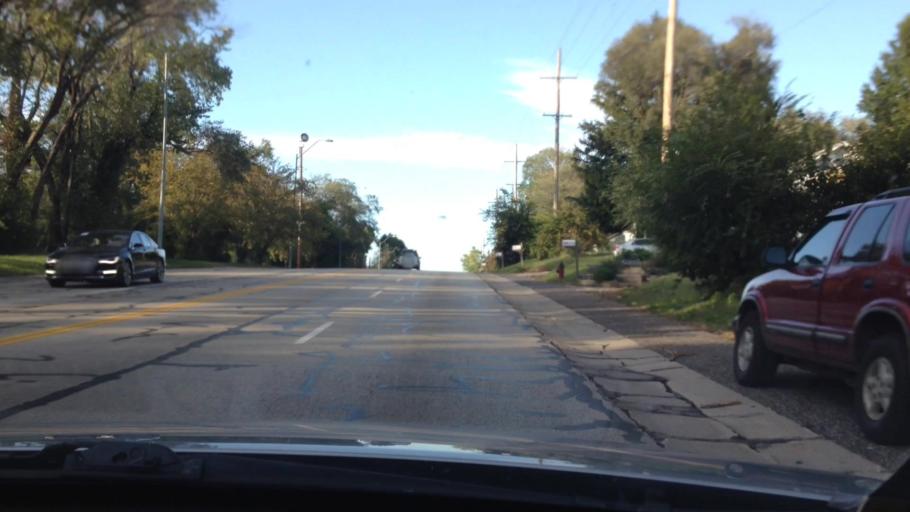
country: US
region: Missouri
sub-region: Clay County
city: Gladstone
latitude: 39.1749
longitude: -94.5767
